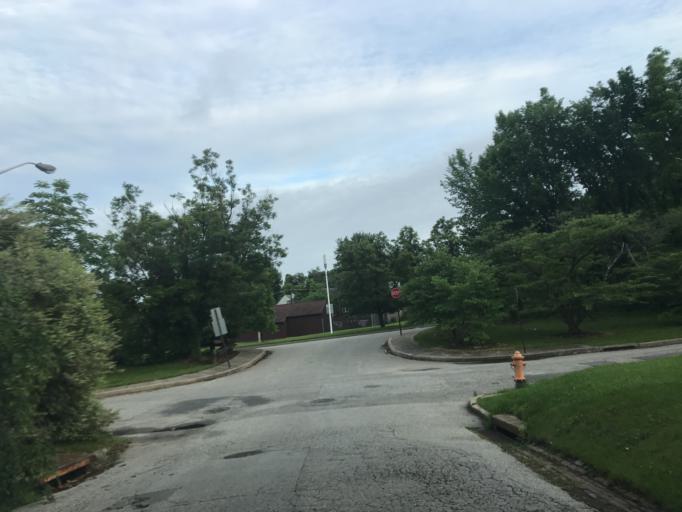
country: US
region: Maryland
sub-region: Baltimore County
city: Towson
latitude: 39.3657
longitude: -76.6135
